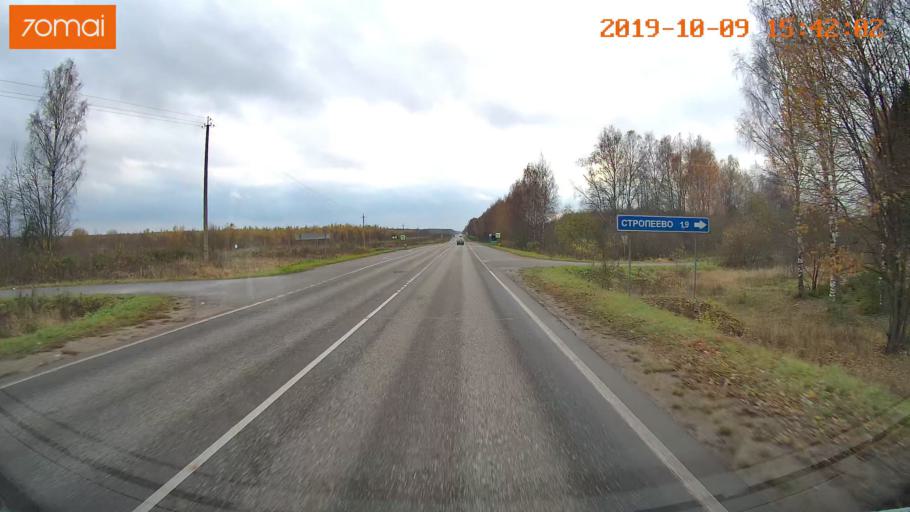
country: RU
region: Kostroma
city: Oktyabr'skiy
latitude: 57.8726
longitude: 41.1142
